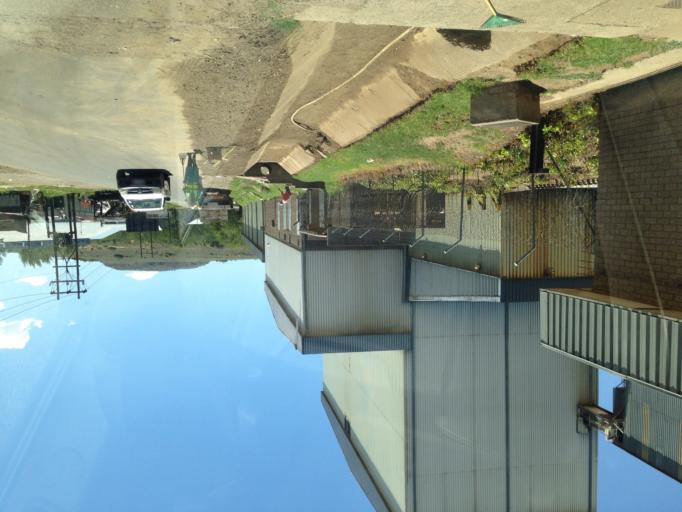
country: LS
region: Maseru
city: Maseru
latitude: -29.2962
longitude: 27.4825
